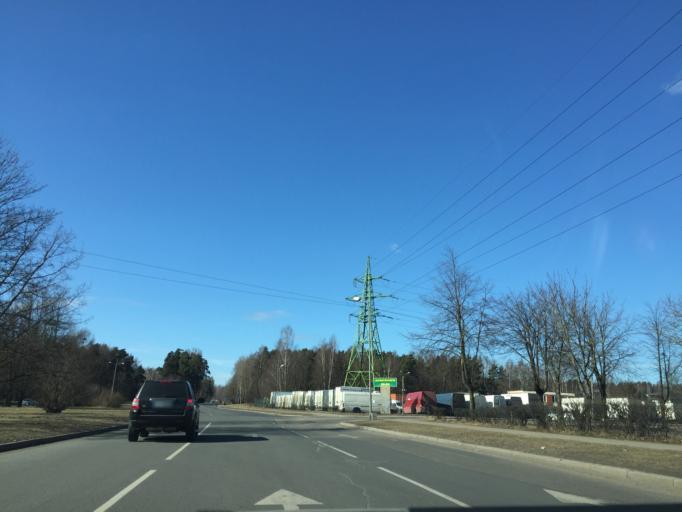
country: LV
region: Marupe
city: Marupe
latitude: 56.9650
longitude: 24.0266
